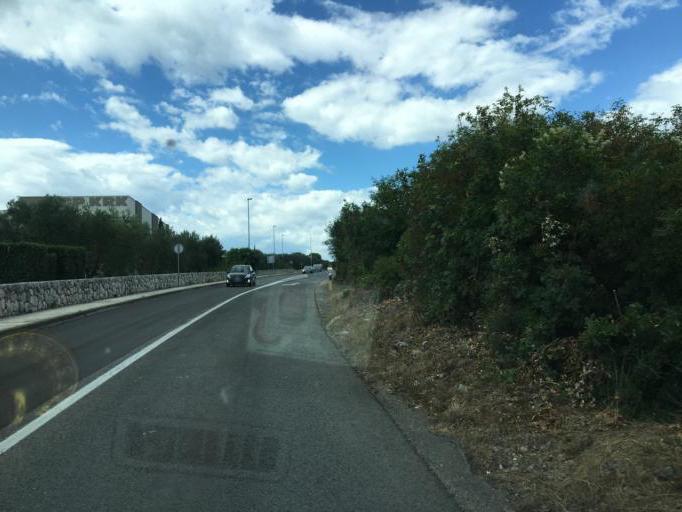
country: HR
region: Primorsko-Goranska
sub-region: Grad Krk
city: Krk
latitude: 45.0366
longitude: 14.5696
